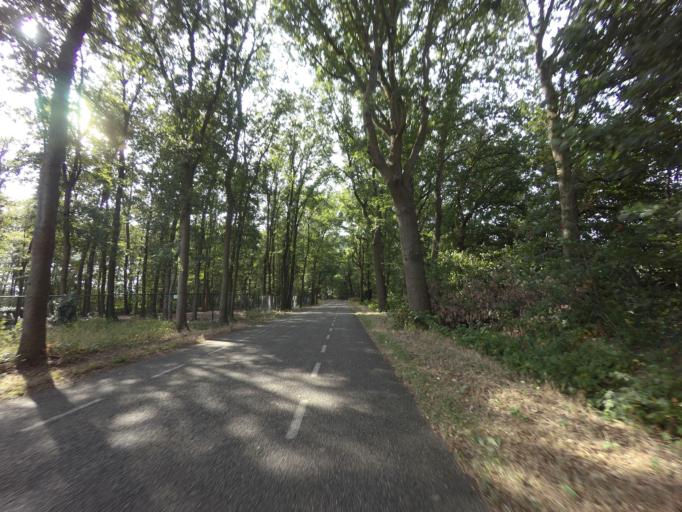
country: NL
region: North Brabant
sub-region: Gemeente Mill en Sint Hubert
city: Wilbertoord
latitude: 51.6428
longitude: 5.8150
